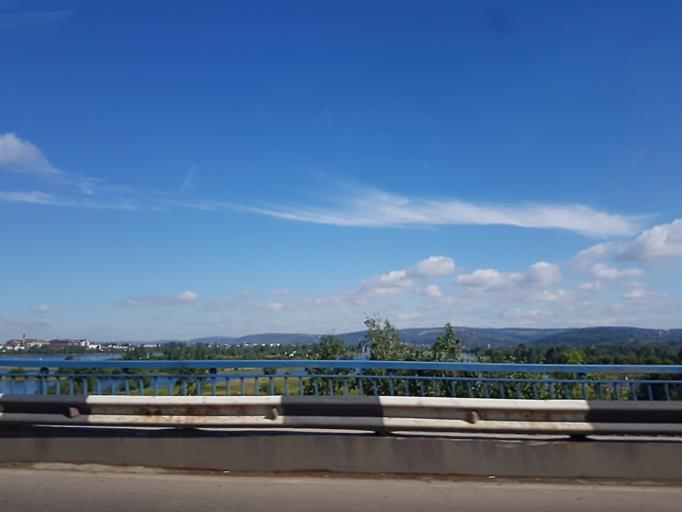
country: RU
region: Irkutsk
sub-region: Irkutskiy Rayon
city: Irkutsk
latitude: 52.3271
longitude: 104.2811
